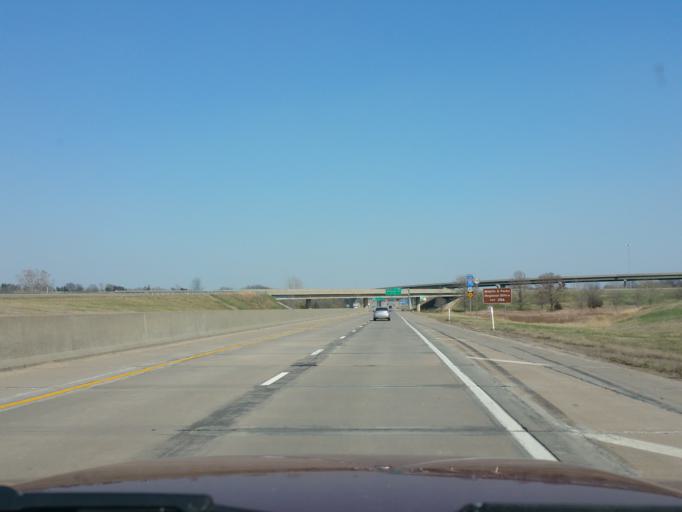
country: US
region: Kansas
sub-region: Shawnee County
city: Silver Lake
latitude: 39.0534
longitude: -95.7777
